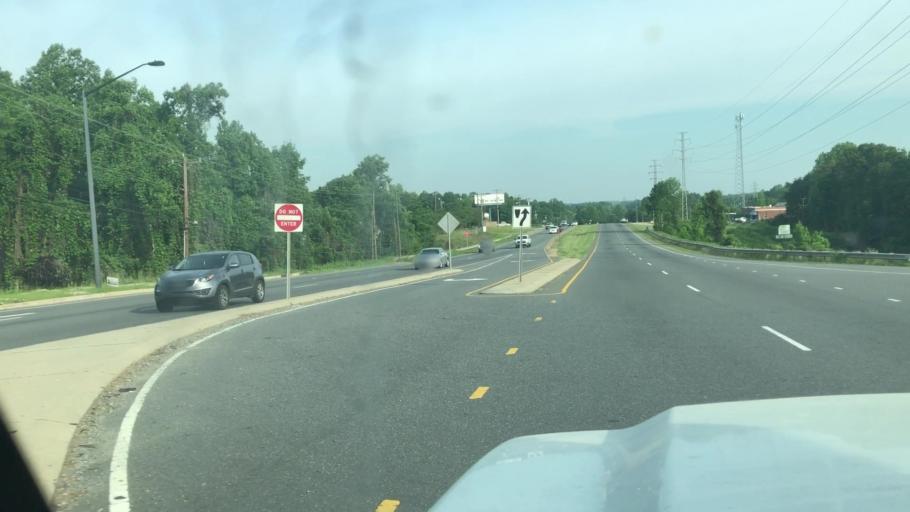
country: US
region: North Carolina
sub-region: Mecklenburg County
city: Charlotte
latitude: 35.2913
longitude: -80.9135
